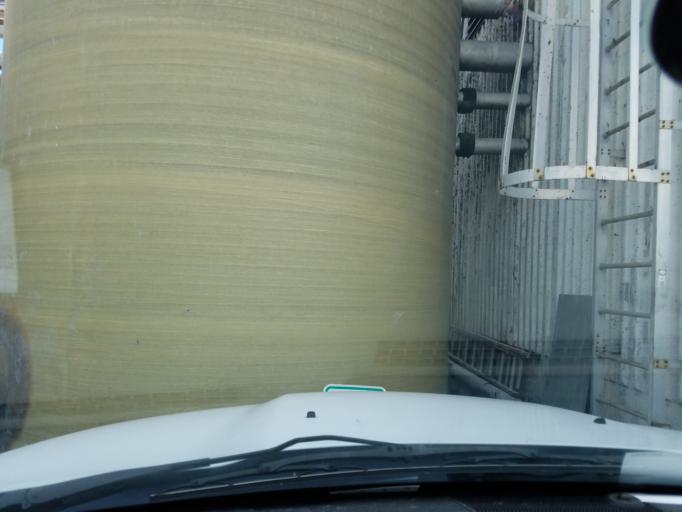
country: US
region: Kentucky
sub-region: Laurel County
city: North Corbin
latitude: 37.0349
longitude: -84.0668
